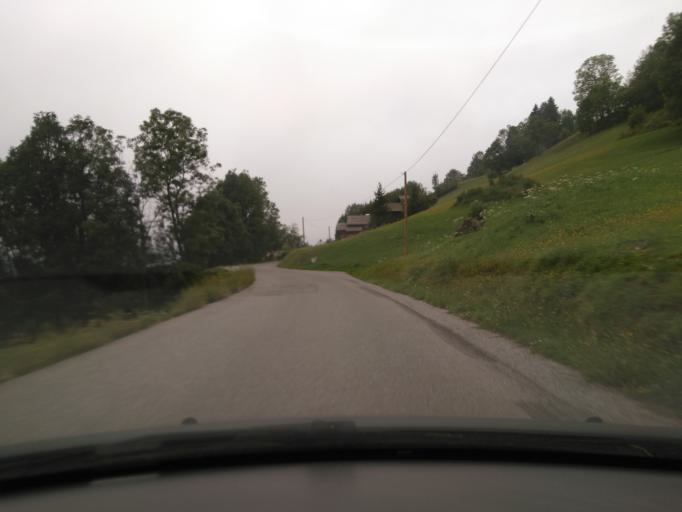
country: FR
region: Rhone-Alpes
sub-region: Departement de la Haute-Savoie
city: La Clusaz
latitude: 45.9134
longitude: 6.4520
